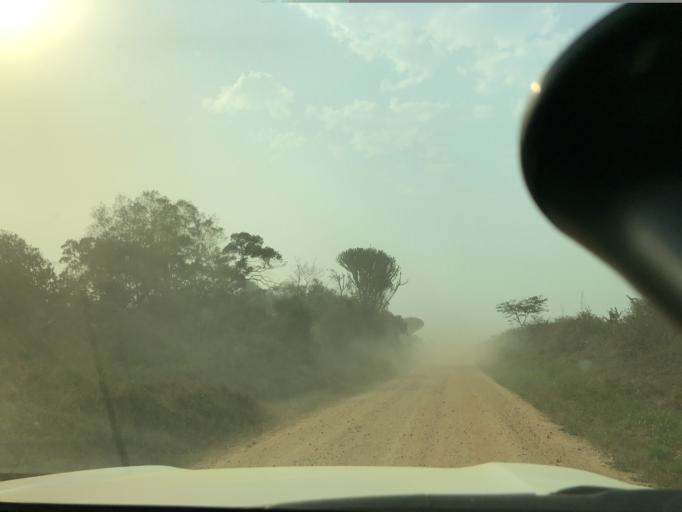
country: CD
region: Nord Kivu
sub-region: North Kivu
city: Butembo
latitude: 0.0831
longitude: 29.6481
